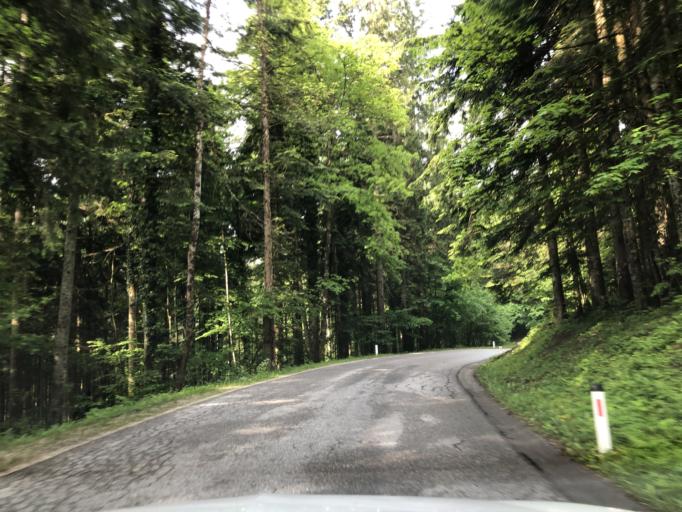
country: SI
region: Velike Lasce
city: Velike Lasce
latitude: 45.8080
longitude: 14.6201
